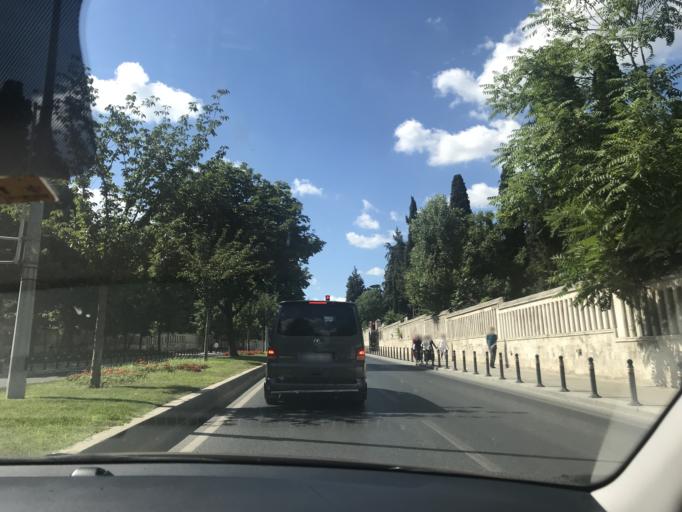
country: TR
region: Istanbul
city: UEskuedar
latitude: 41.0100
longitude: 29.0221
